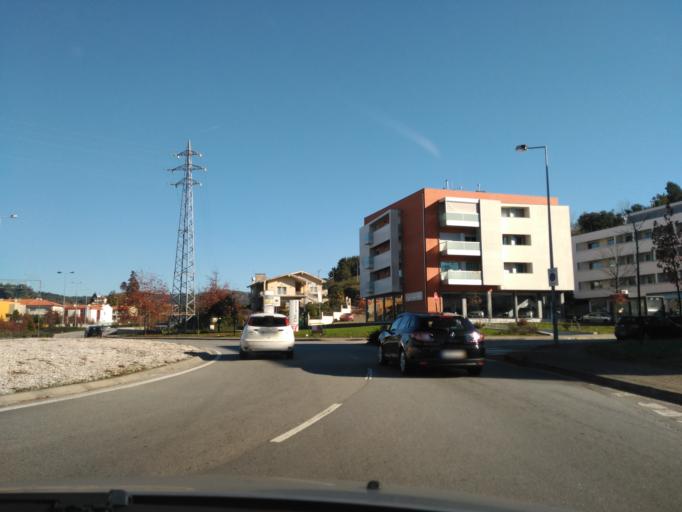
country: PT
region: Braga
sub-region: Braga
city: Adaufe
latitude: 41.5626
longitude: -8.3840
